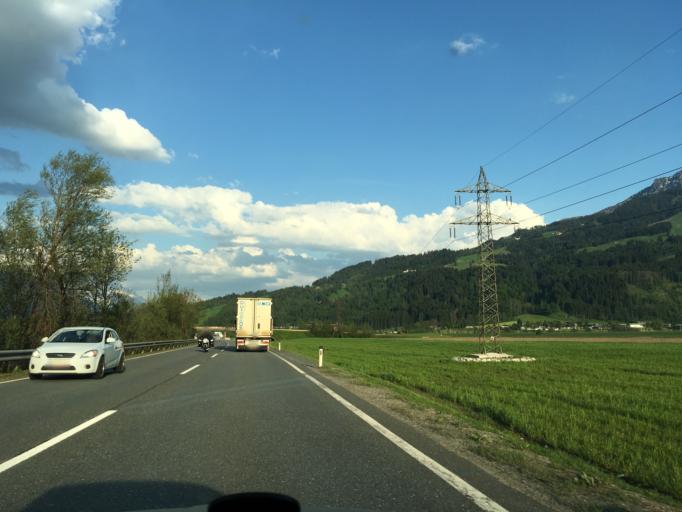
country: AT
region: Tyrol
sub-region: Politischer Bezirk Kitzbuhel
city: Oberndorf in Tirol
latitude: 47.5202
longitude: 12.3981
